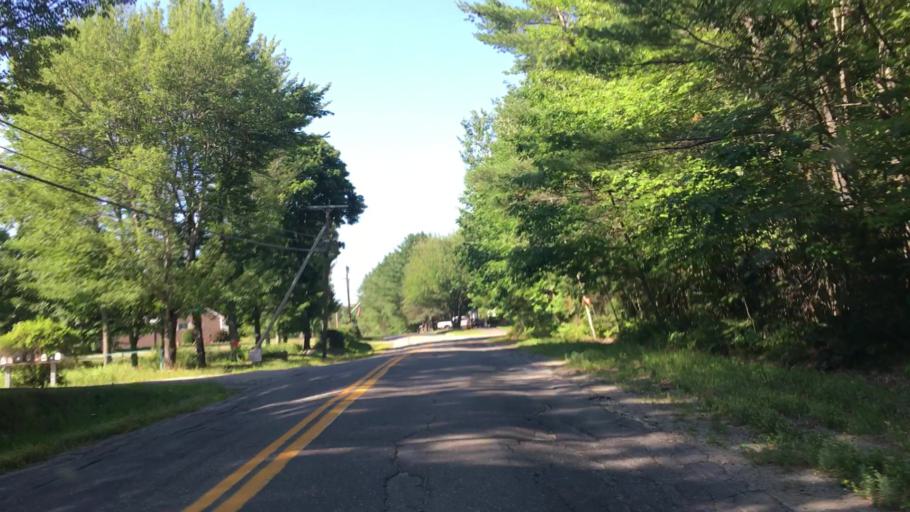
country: US
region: Maine
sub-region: Penobscot County
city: Enfield
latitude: 45.2543
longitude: -68.5645
